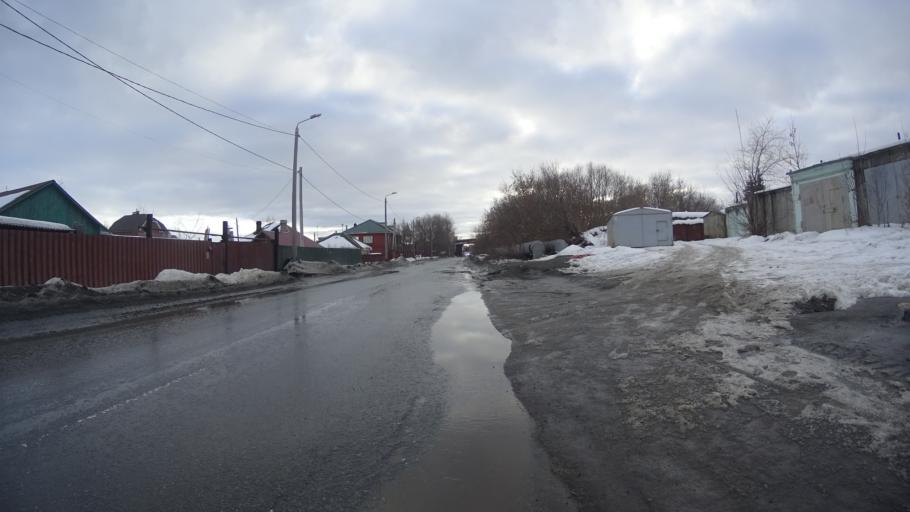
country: RU
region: Chelyabinsk
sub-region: Gorod Chelyabinsk
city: Chelyabinsk
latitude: 55.1373
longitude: 61.3936
